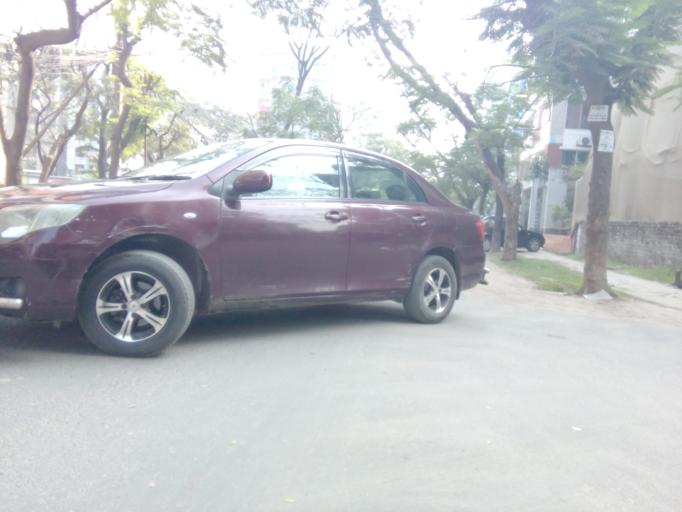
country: BD
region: Dhaka
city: Tungi
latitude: 23.8205
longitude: 90.4338
